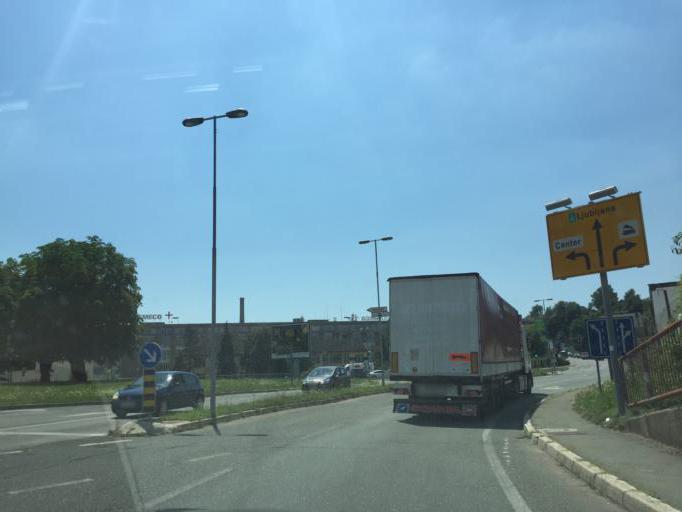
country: SI
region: Kranj
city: Kranj
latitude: 46.2384
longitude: 14.3506
